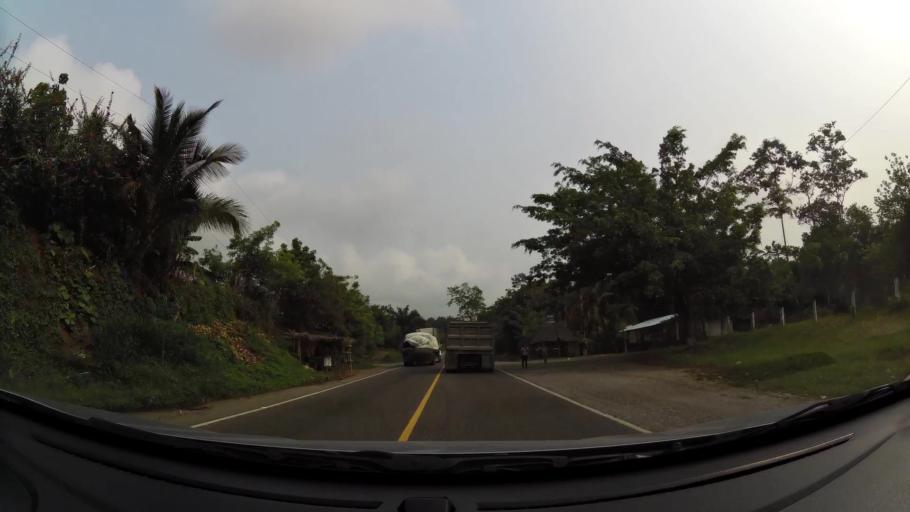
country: HN
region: Atlantida
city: Mezapa
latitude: 15.6243
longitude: -87.6179
